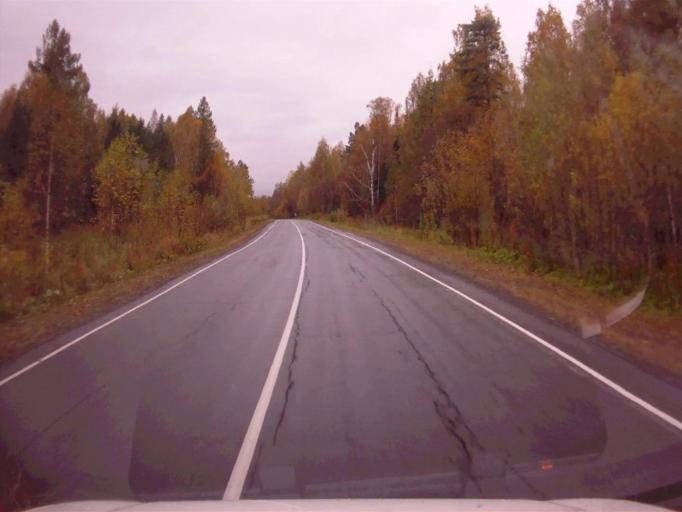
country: RU
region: Chelyabinsk
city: Nizhniy Ufaley
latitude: 56.0663
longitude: 60.0046
